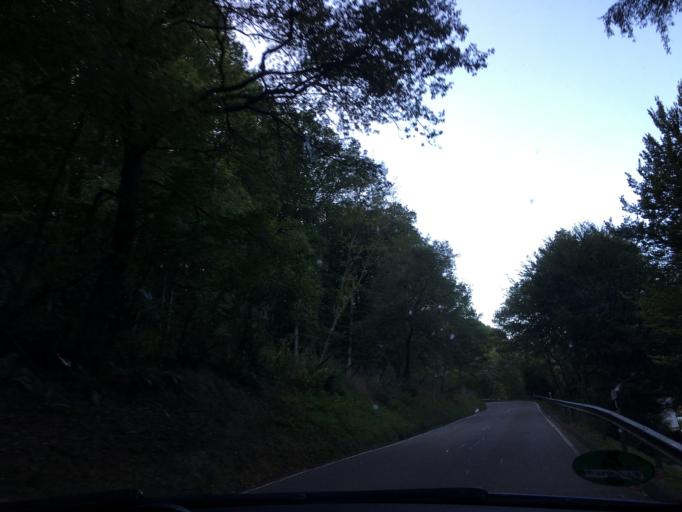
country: DE
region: Rheinland-Pfalz
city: Steinalben
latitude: 49.3130
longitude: 7.6502
